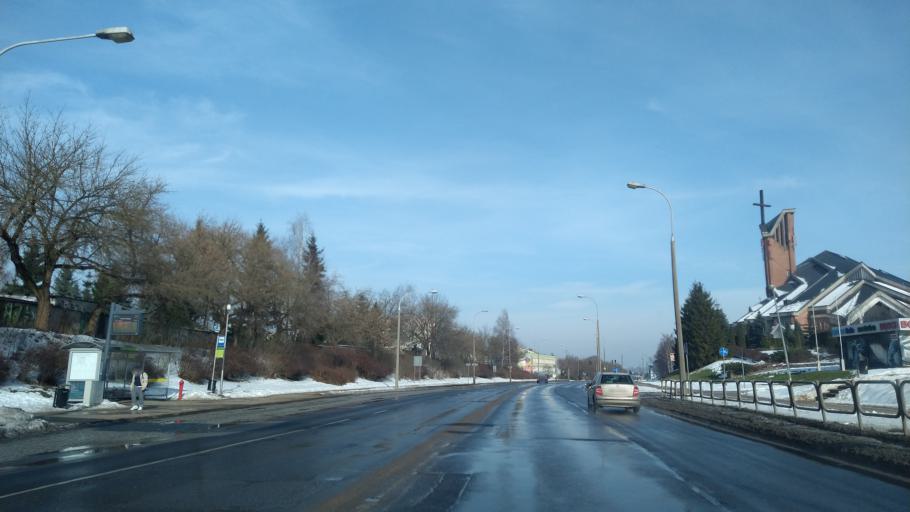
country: PL
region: Warmian-Masurian Voivodeship
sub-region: Powiat olsztynski
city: Olsztyn
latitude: 53.7642
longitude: 20.5020
